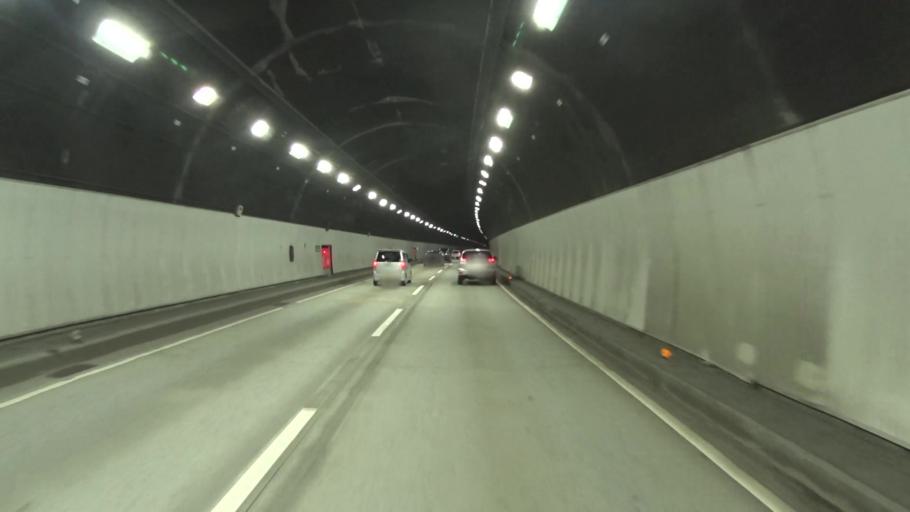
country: JP
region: Shiga Prefecture
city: Otsu-shi
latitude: 35.0184
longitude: 135.8474
